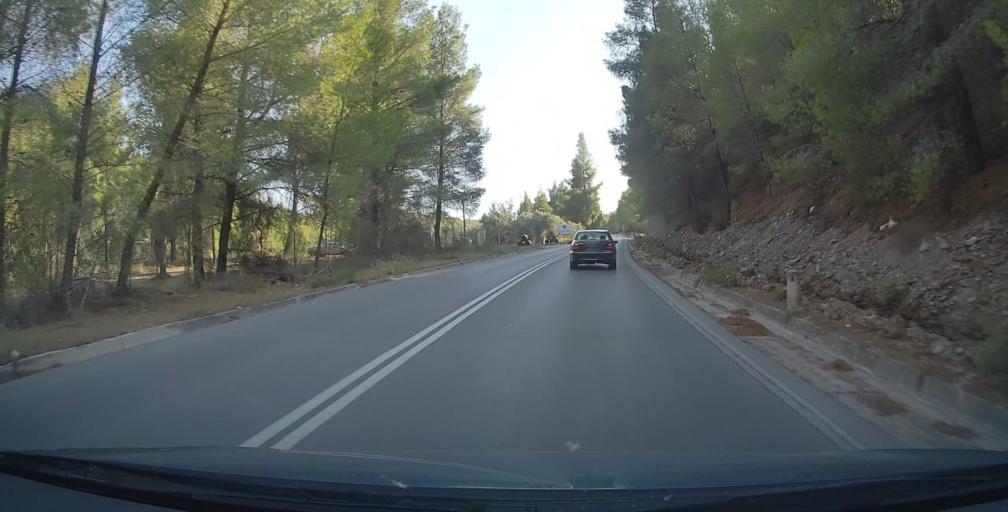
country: GR
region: Central Macedonia
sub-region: Nomos Chalkidikis
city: Neos Marmaras
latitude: 40.0729
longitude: 23.8061
